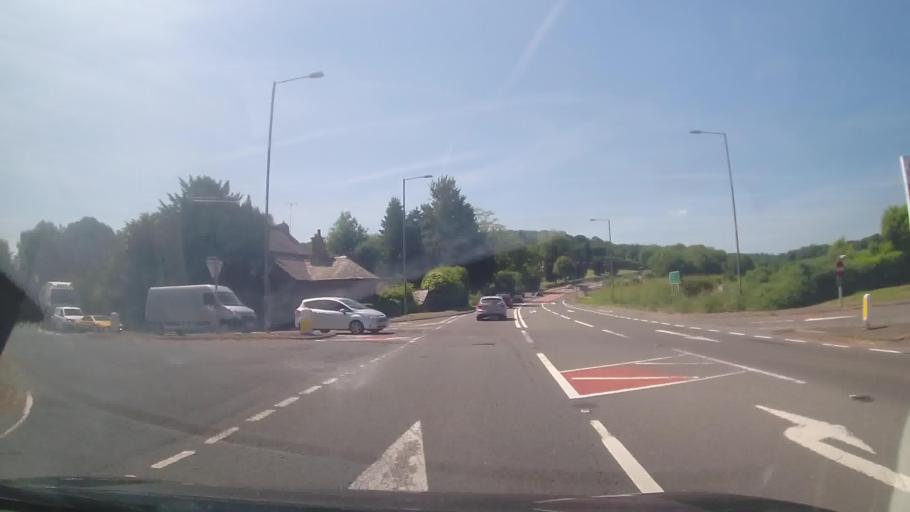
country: GB
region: England
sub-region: Herefordshire
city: Hope under Dinmore
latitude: 52.1742
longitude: -2.7151
